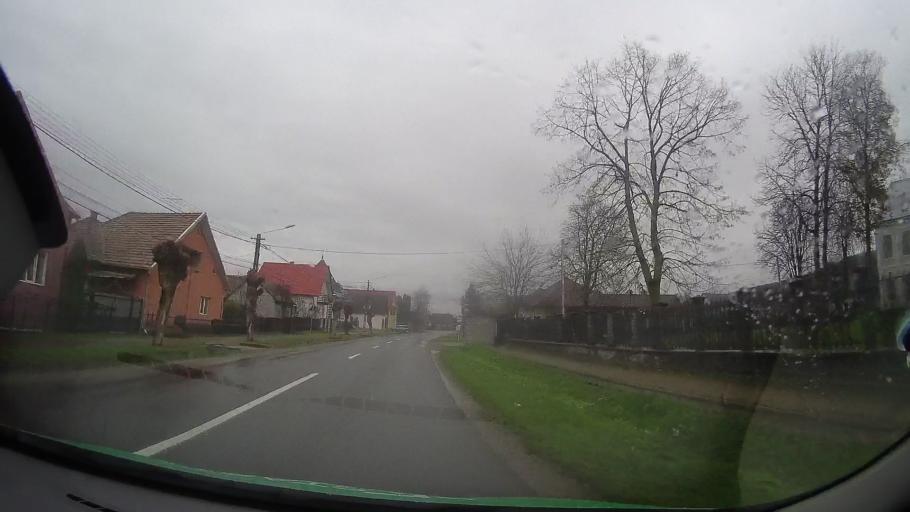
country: RO
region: Bistrita-Nasaud
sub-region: Municipiul Bistrita
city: Viisoara
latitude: 47.0772
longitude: 24.4371
